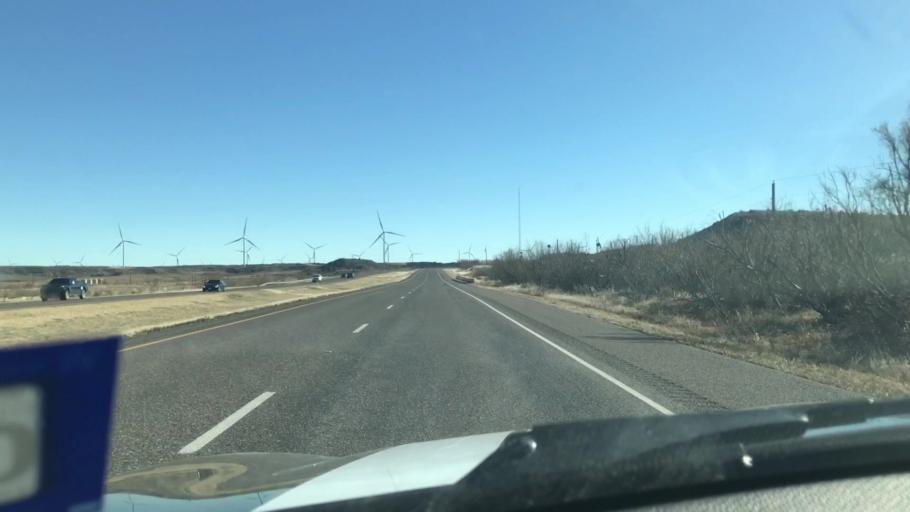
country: US
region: Texas
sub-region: Scurry County
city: Snyder
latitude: 32.9212
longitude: -101.0624
